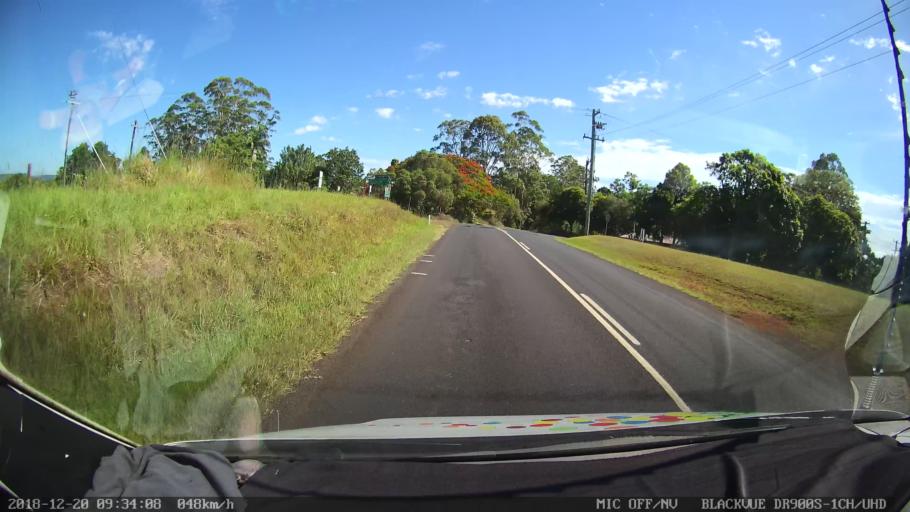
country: AU
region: New South Wales
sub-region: Lismore Municipality
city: Goonellabah
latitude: -28.6922
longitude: 153.3126
